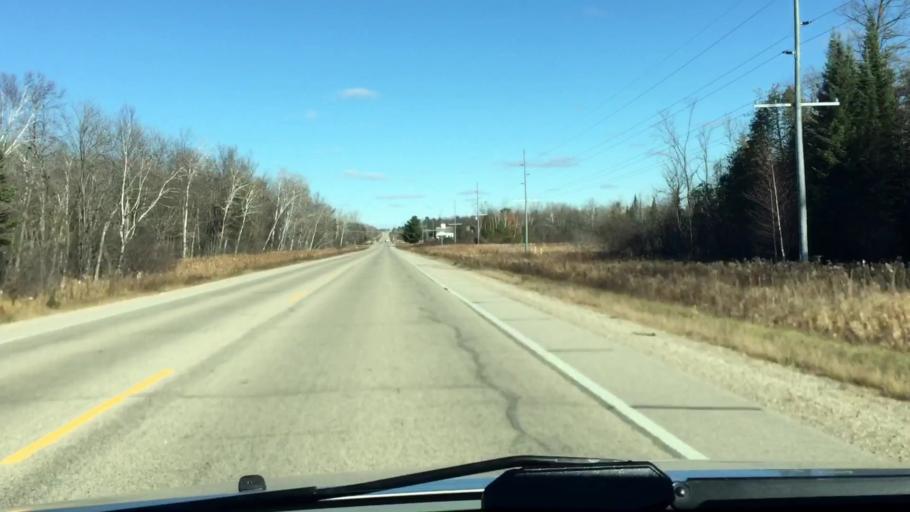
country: US
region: Wisconsin
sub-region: Oconto County
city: Gillett
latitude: 44.8760
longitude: -88.2473
